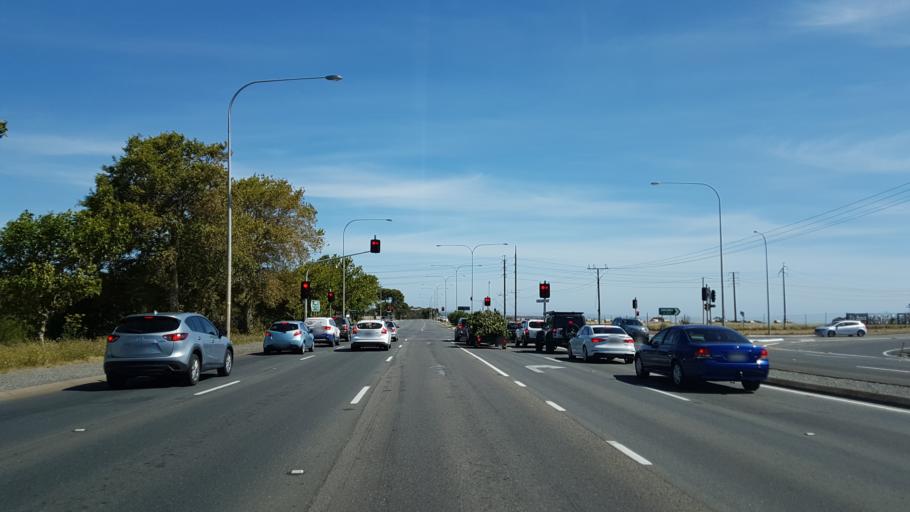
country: AU
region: South Australia
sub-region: Onkaparinga
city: Bedford Park
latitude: -35.0530
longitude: 138.5596
